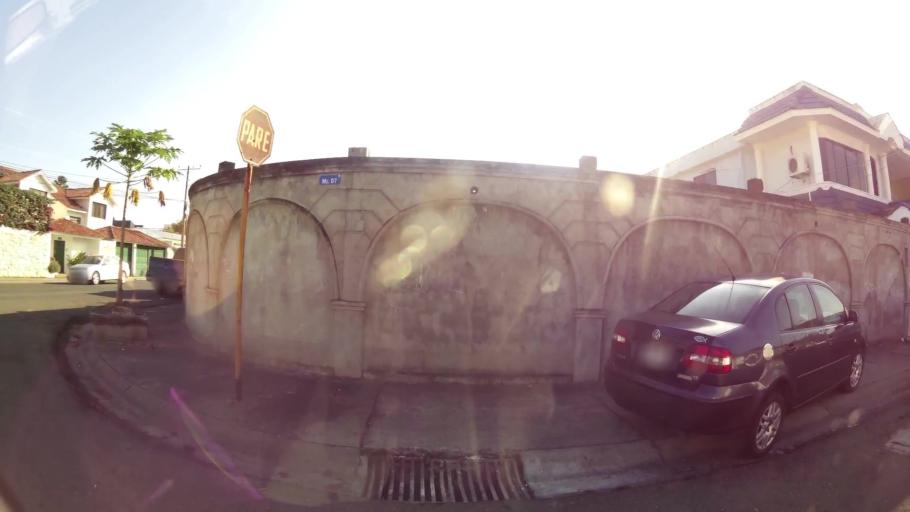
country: EC
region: Guayas
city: Santa Lucia
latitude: -2.1899
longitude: -79.9636
